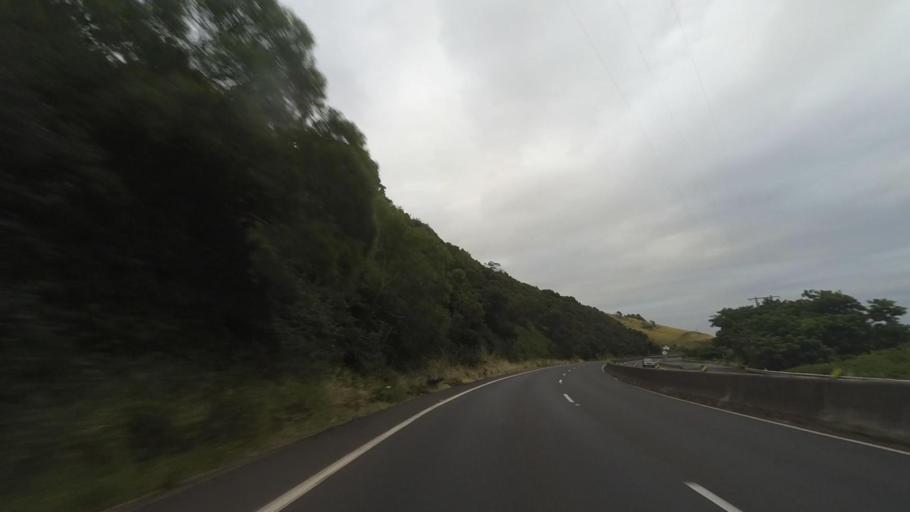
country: AU
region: New South Wales
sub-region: Kiama
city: Gerringong
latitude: -34.7077
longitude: 150.8394
